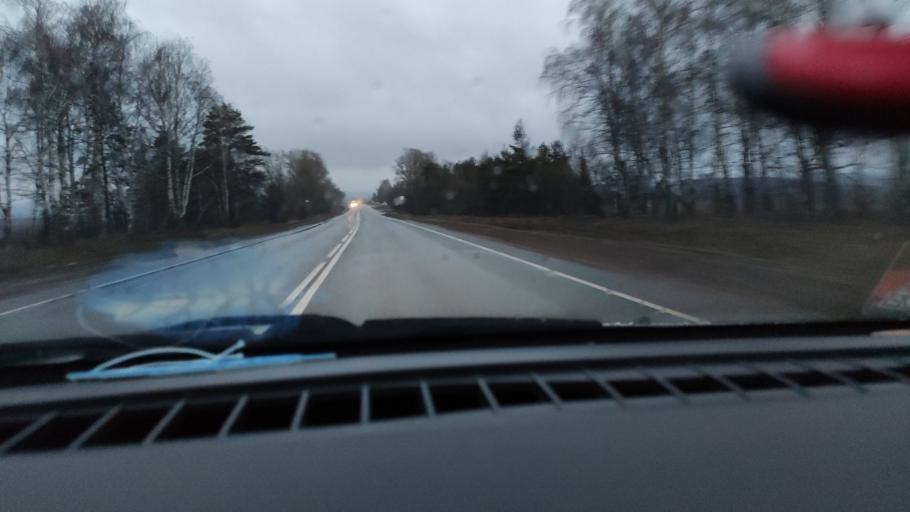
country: RU
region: Udmurtiya
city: Alnashi
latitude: 56.2190
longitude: 52.4227
